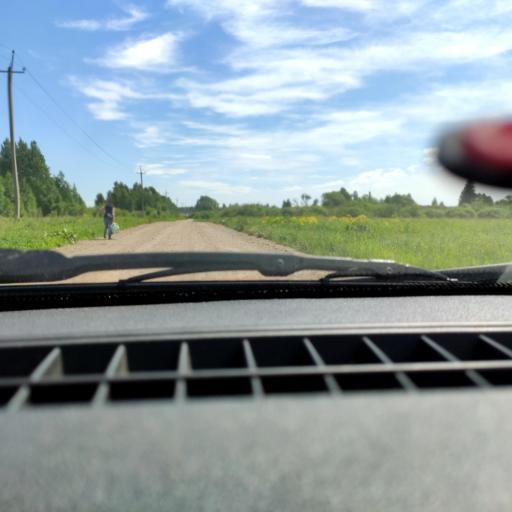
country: RU
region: Bashkortostan
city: Kabakovo
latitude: 54.7297
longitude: 56.2016
